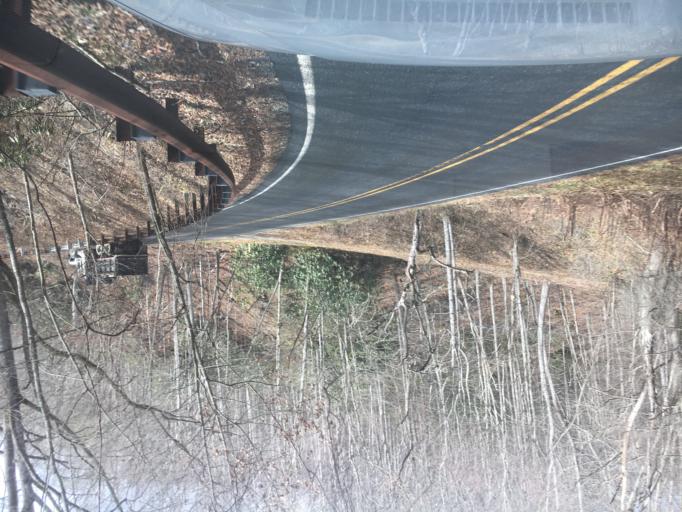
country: US
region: North Carolina
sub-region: Haywood County
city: Canton
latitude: 35.3753
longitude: -82.8142
